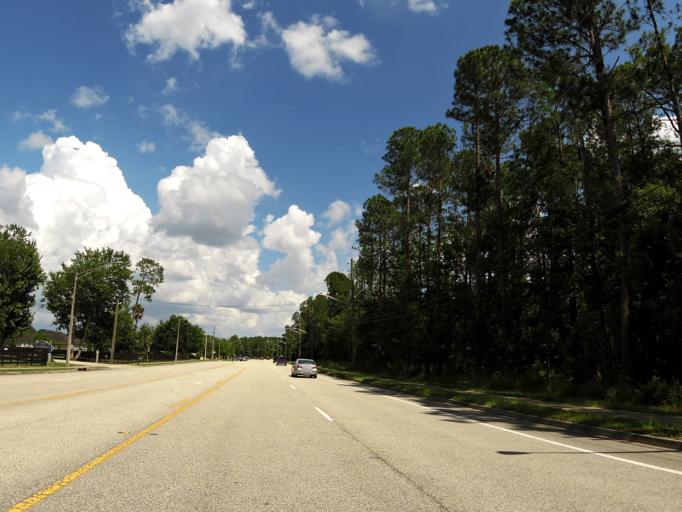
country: US
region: Florida
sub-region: Saint Johns County
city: Fruit Cove
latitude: 30.1511
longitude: -81.5820
